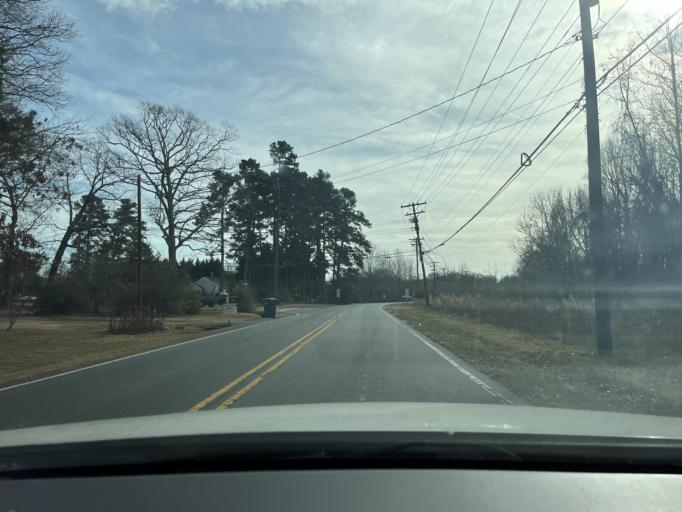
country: US
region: North Carolina
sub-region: Guilford County
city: Pleasant Garden
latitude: 36.0146
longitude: -79.7762
